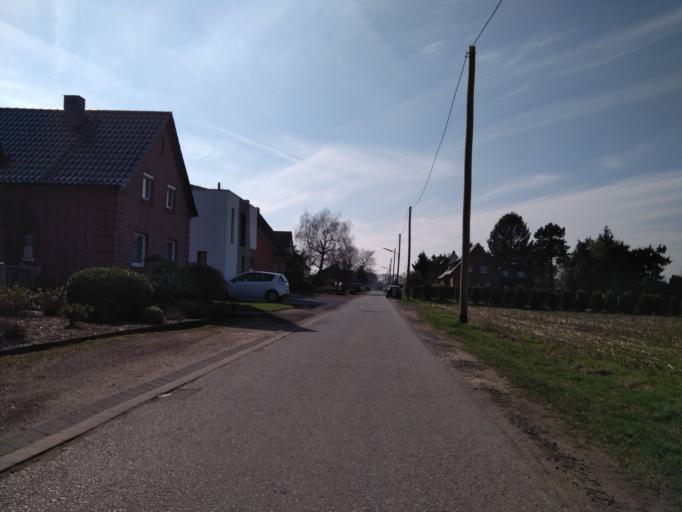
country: DE
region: North Rhine-Westphalia
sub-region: Regierungsbezirk Munster
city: Gladbeck
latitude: 51.6076
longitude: 6.9644
